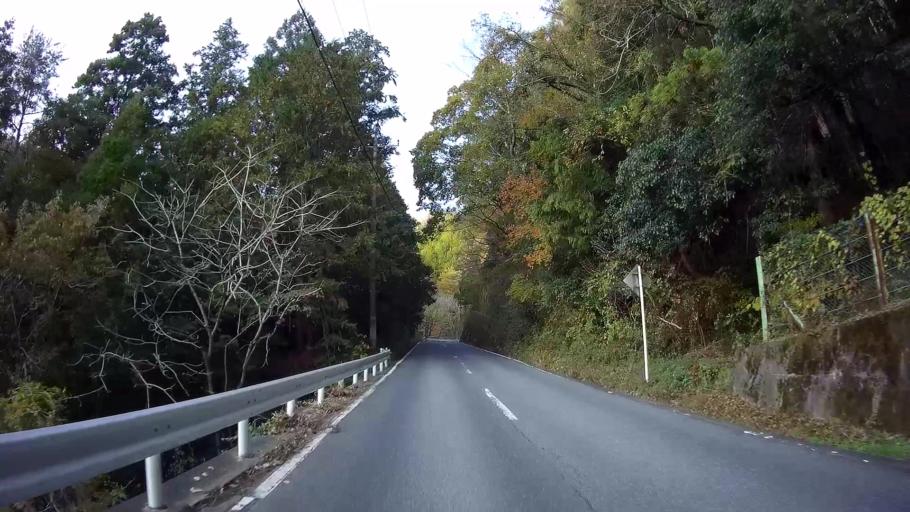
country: JP
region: Yamanashi
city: Ryuo
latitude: 35.4682
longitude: 138.4880
